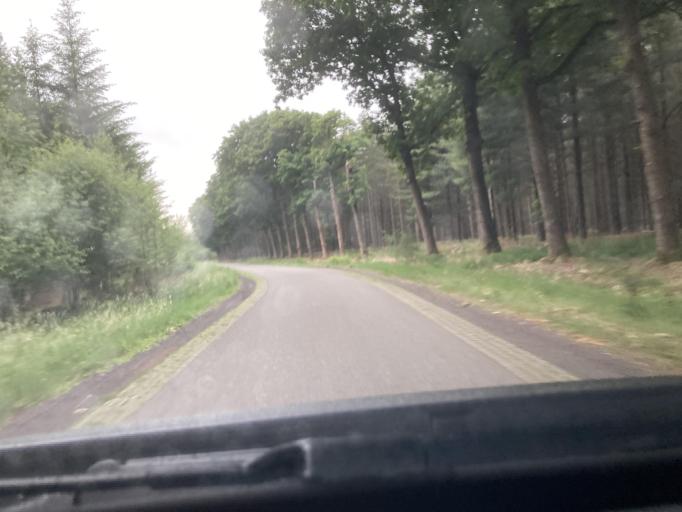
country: NL
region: North Brabant
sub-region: Gemeente Hilvarenbeek
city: Hilvarenbeek
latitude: 51.4274
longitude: 5.1149
